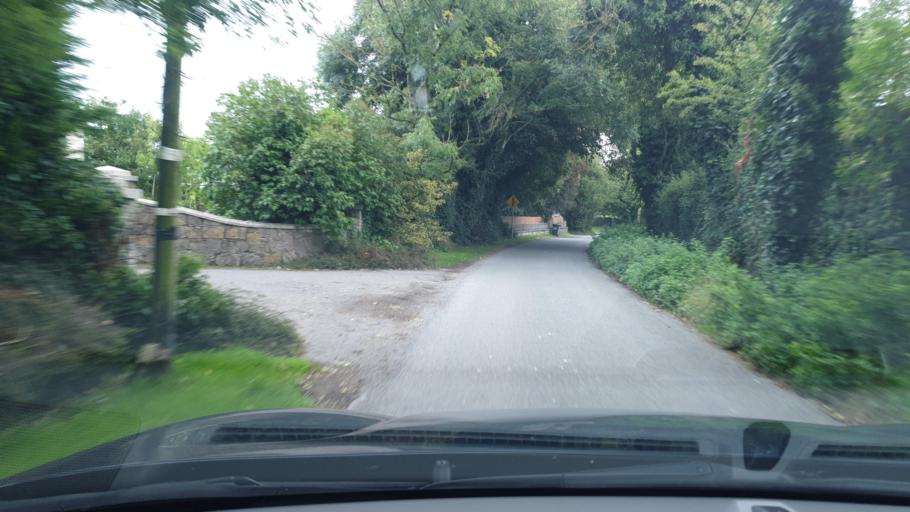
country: IE
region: Leinster
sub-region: An Mhi
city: Dunshaughlin
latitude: 53.4889
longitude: -6.5907
